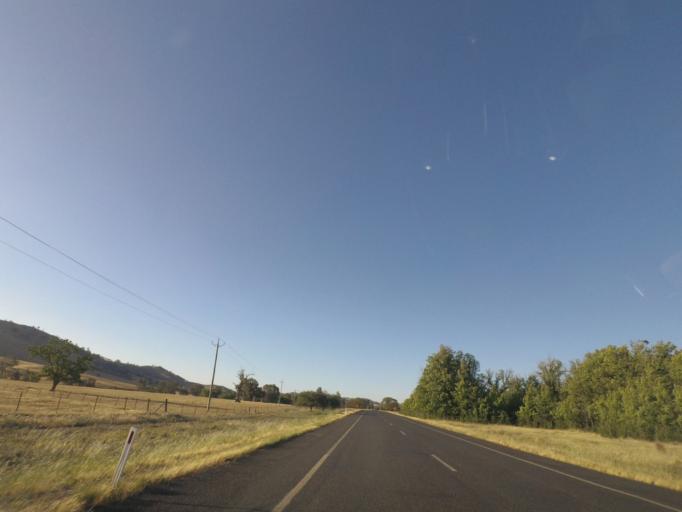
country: AU
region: New South Wales
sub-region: Gundagai
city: Gundagai
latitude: -34.9385
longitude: 148.1677
